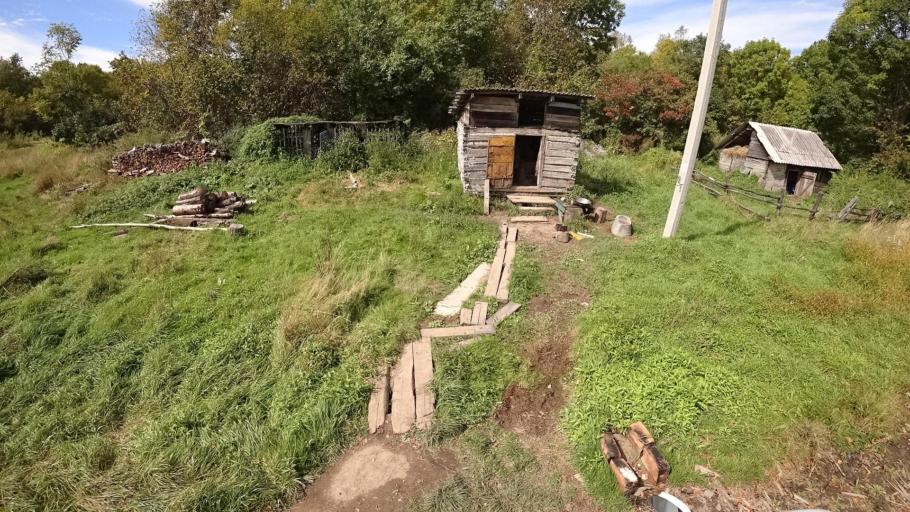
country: RU
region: Primorskiy
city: Yakovlevka
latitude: 44.7120
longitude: 133.6298
